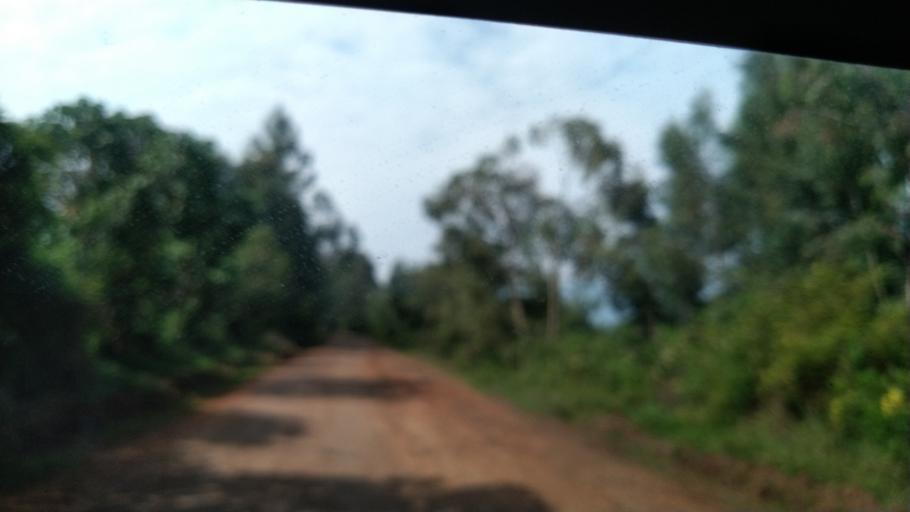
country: ET
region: Oromiya
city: Jima
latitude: 7.6670
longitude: 37.2448
